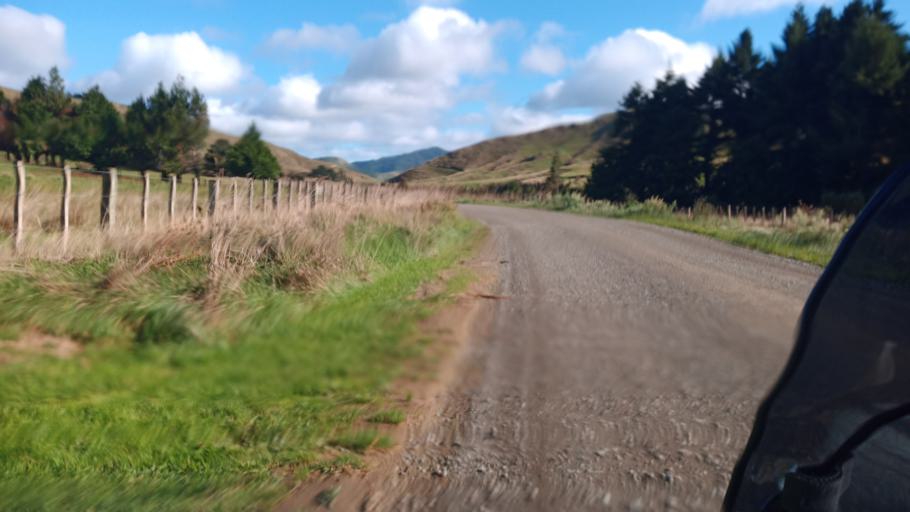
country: NZ
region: Bay of Plenty
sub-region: Opotiki District
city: Opotiki
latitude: -38.4708
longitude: 177.4365
